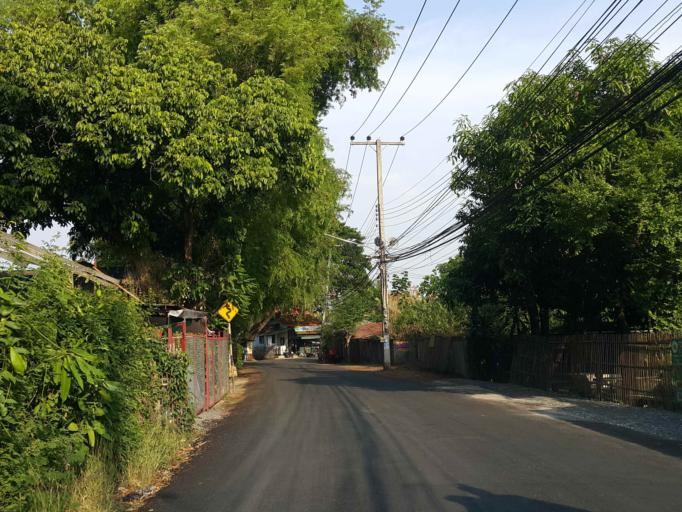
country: TH
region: Chiang Mai
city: Chiang Mai
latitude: 18.7722
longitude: 99.0220
